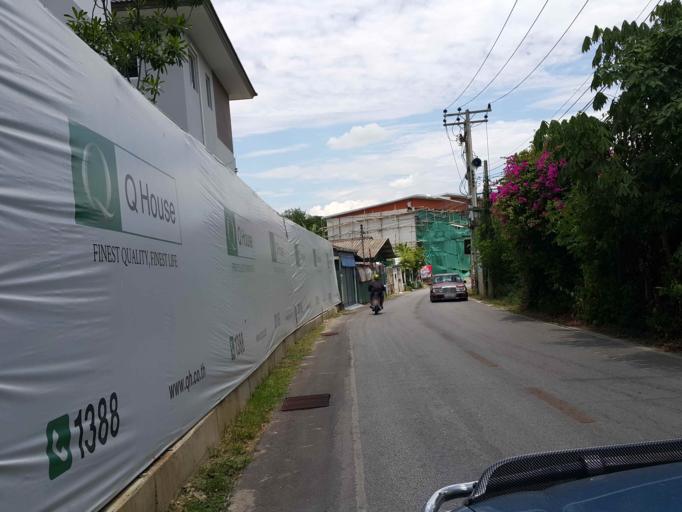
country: TH
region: Chiang Mai
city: Chiang Mai
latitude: 18.7819
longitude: 99.0141
